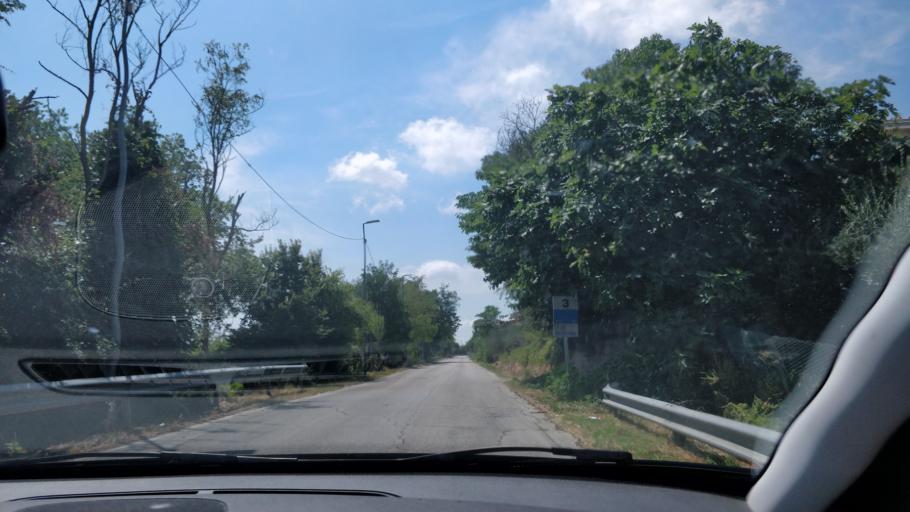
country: IT
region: Abruzzo
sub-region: Provincia di Chieti
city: Sambuceto
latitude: 42.4107
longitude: 14.2053
